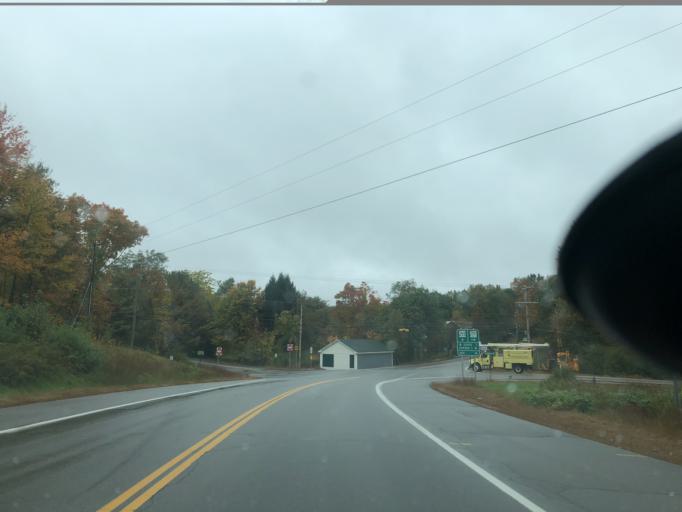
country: US
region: New Hampshire
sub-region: Strafford County
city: Lee
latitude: 43.1499
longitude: -70.9765
